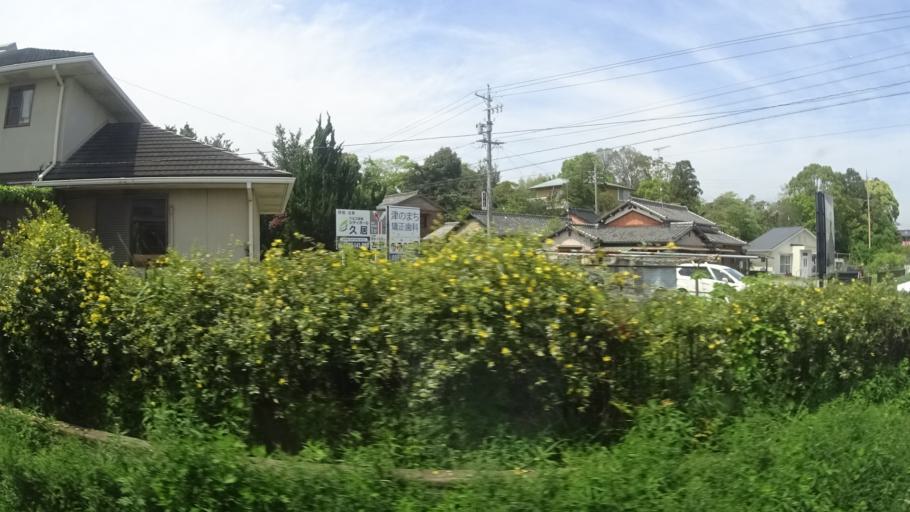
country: JP
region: Mie
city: Tsu-shi
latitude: 34.7013
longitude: 136.5054
